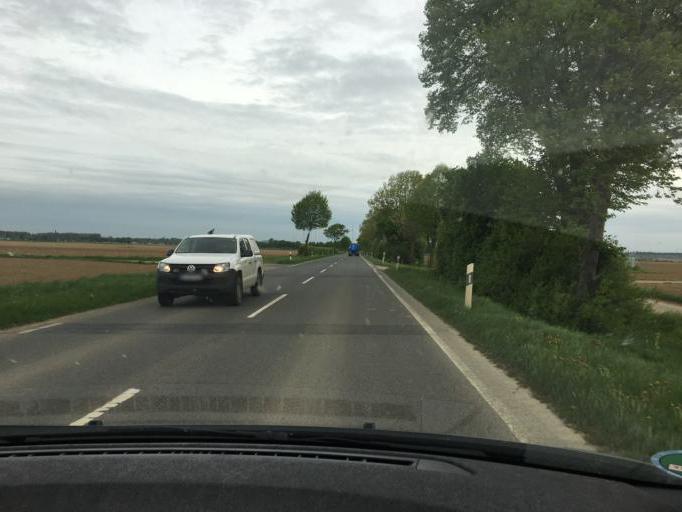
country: DE
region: North Rhine-Westphalia
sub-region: Regierungsbezirk Koln
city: Titz
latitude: 51.0648
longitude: 6.4276
